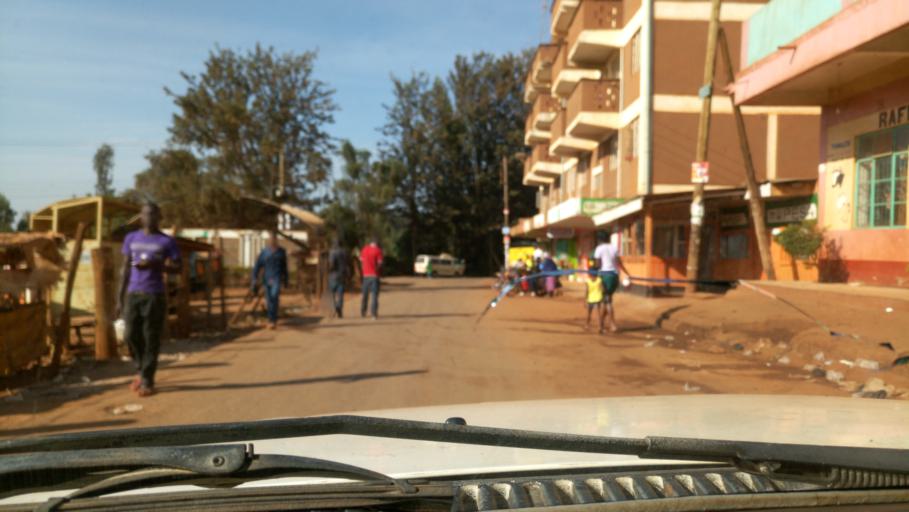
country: KE
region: Murang'a District
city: Murang'a
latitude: -0.7324
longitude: 37.1493
